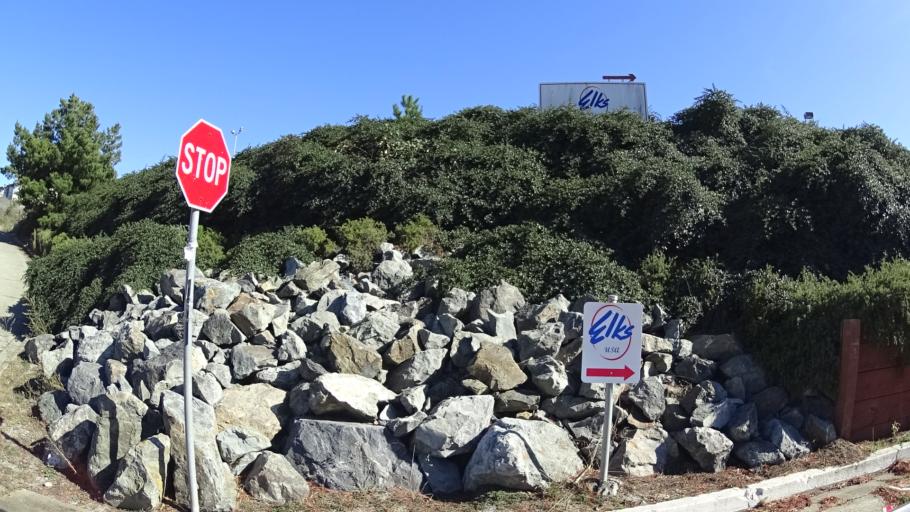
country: US
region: California
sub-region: San Mateo County
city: South San Francisco
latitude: 37.6663
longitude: -122.4257
